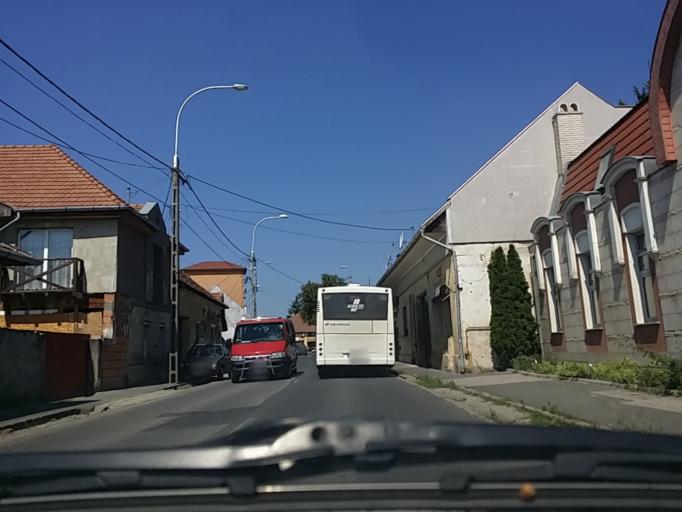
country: HU
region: Pest
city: Nagykovacsi
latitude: 47.6483
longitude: 19.0202
